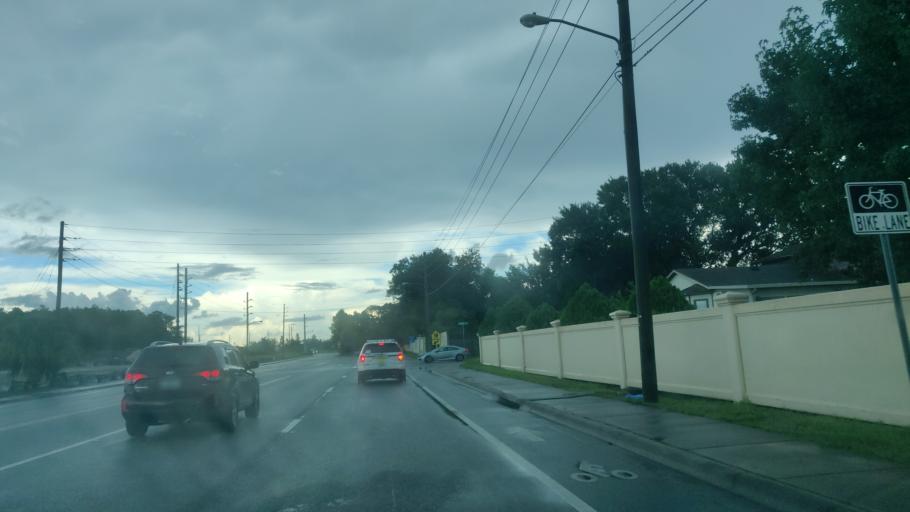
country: US
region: Florida
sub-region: Osceola County
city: Kissimmee
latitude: 28.3192
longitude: -81.4244
